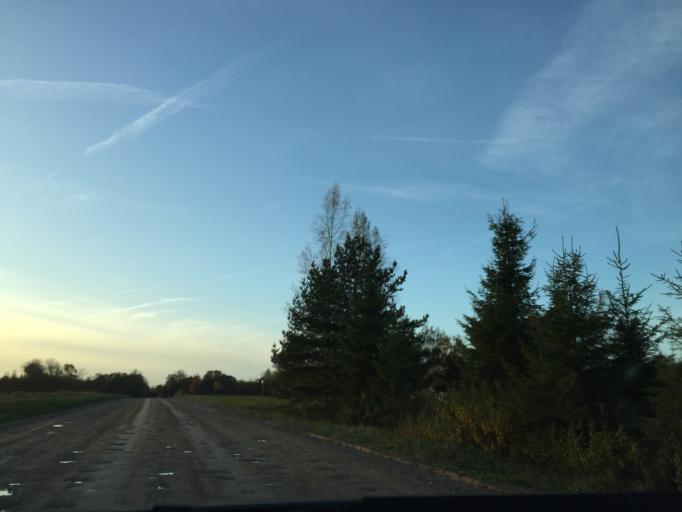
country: LV
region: Malpils
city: Malpils
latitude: 56.8826
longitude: 24.9737
